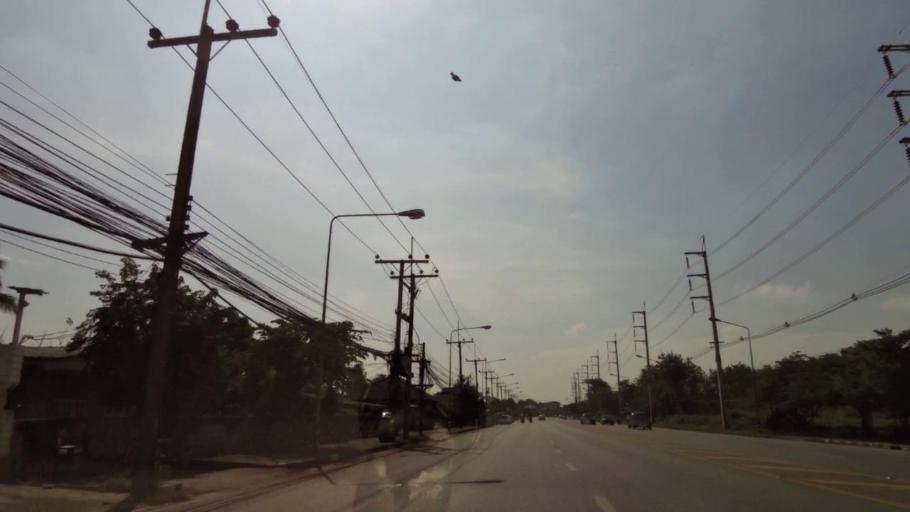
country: TH
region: Chiang Rai
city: Chiang Rai
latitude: 19.8871
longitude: 99.8010
